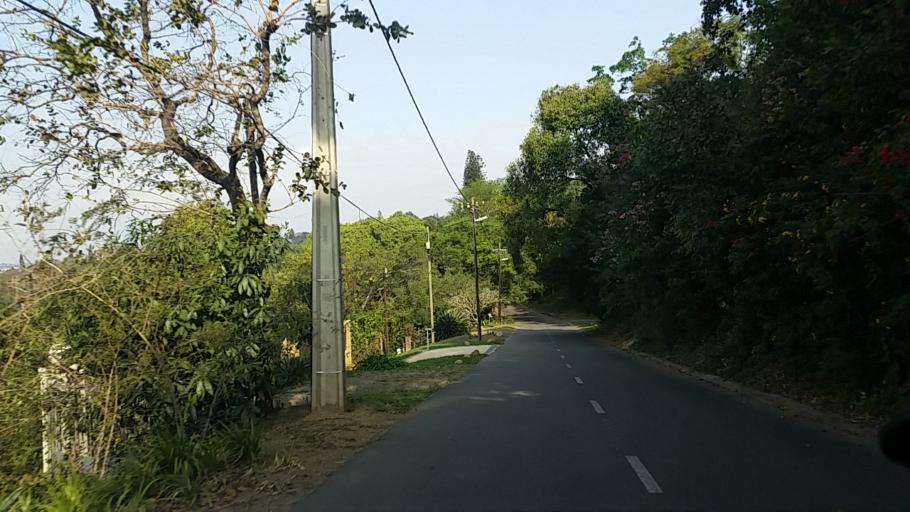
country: ZA
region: KwaZulu-Natal
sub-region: eThekwini Metropolitan Municipality
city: Berea
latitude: -29.8365
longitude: 30.9474
